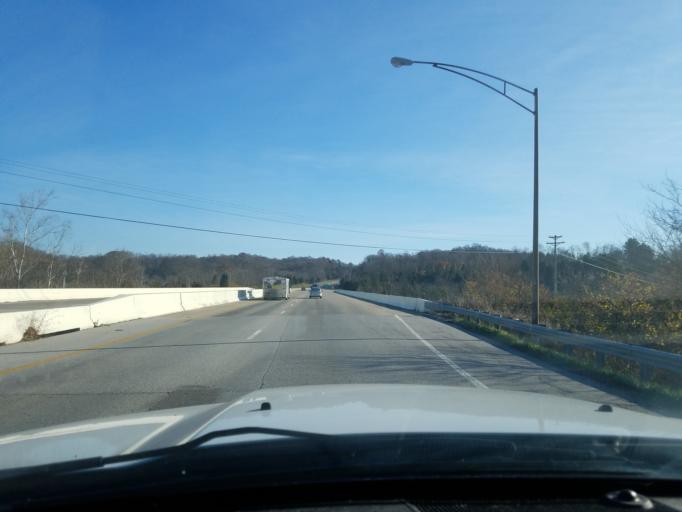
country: US
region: Ohio
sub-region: Clermont County
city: Batavia
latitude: 39.0853
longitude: -84.1802
